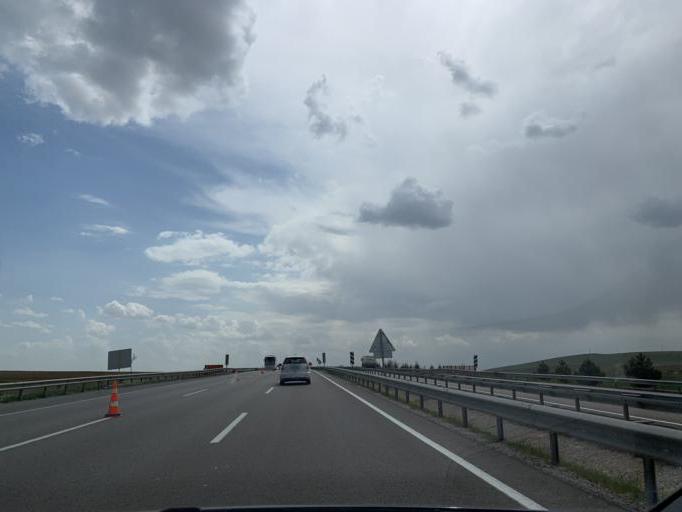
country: TR
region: Ankara
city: Polatli
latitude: 39.6194
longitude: 32.1892
